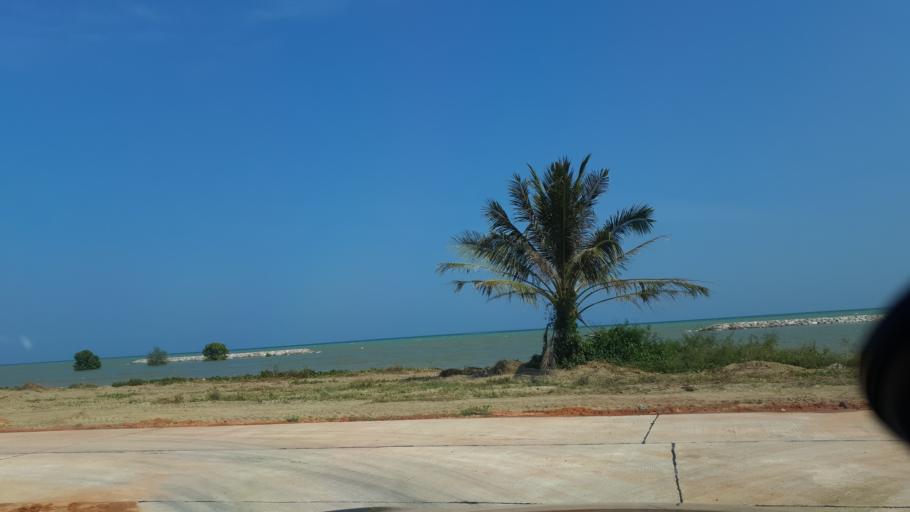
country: TH
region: Surat Thani
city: Tha Chana
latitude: 9.5944
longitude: 99.2086
